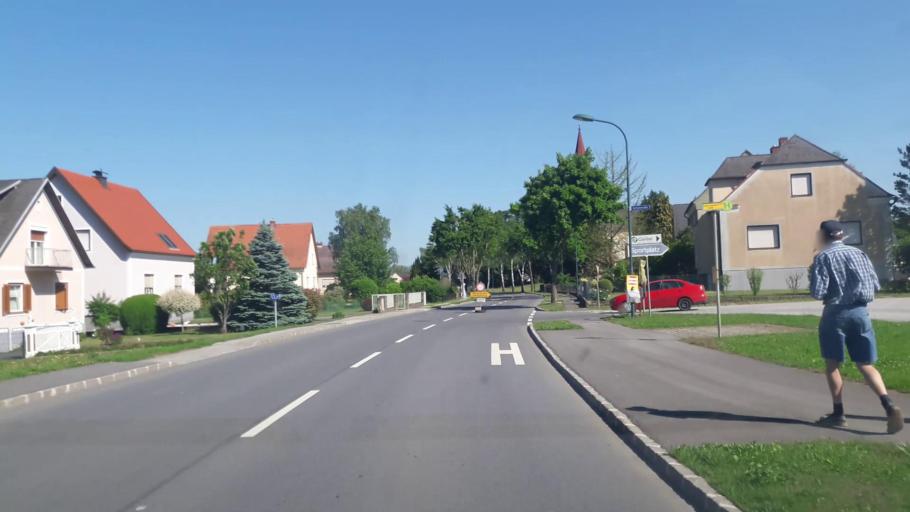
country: AT
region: Burgenland
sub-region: Politischer Bezirk Jennersdorf
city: Deutsch Kaltenbrunn
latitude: 47.0830
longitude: 16.1083
